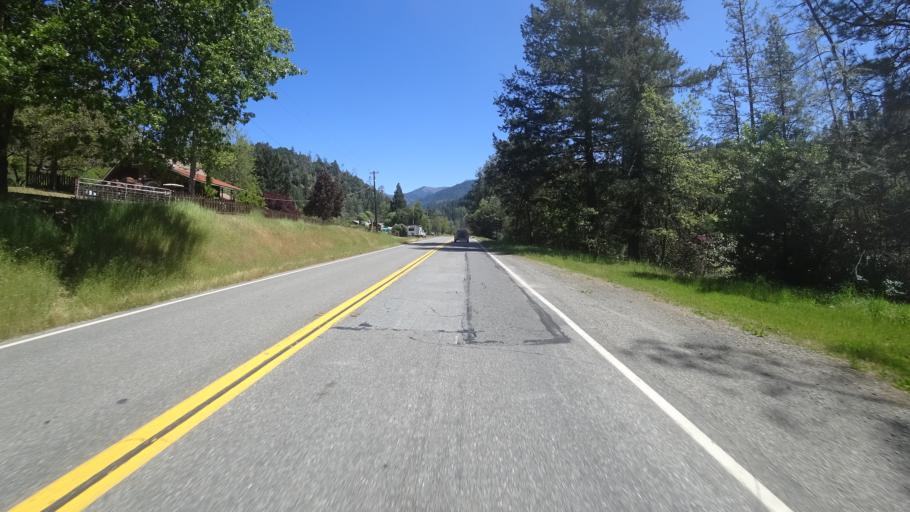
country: US
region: California
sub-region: Trinity County
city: Hayfork
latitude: 40.7413
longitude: -123.2568
